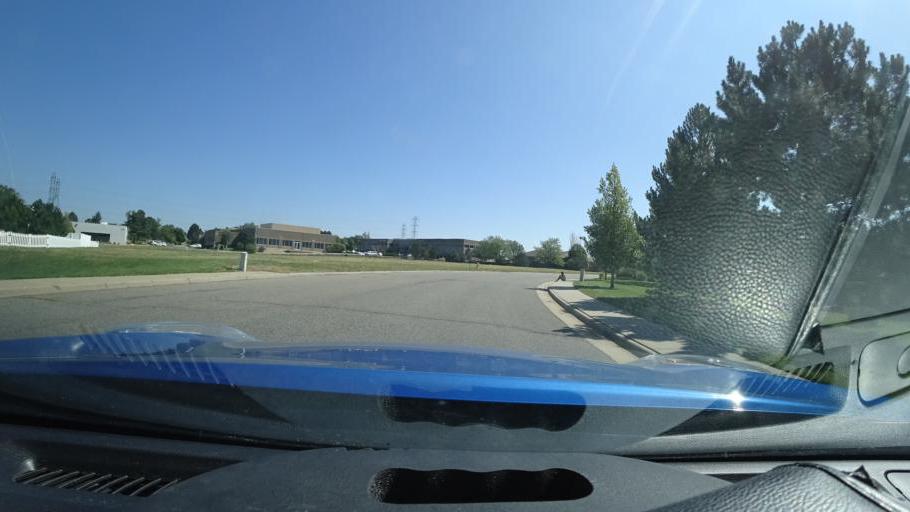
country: US
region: Colorado
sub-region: Adams County
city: Aurora
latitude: 39.6796
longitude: -104.8237
